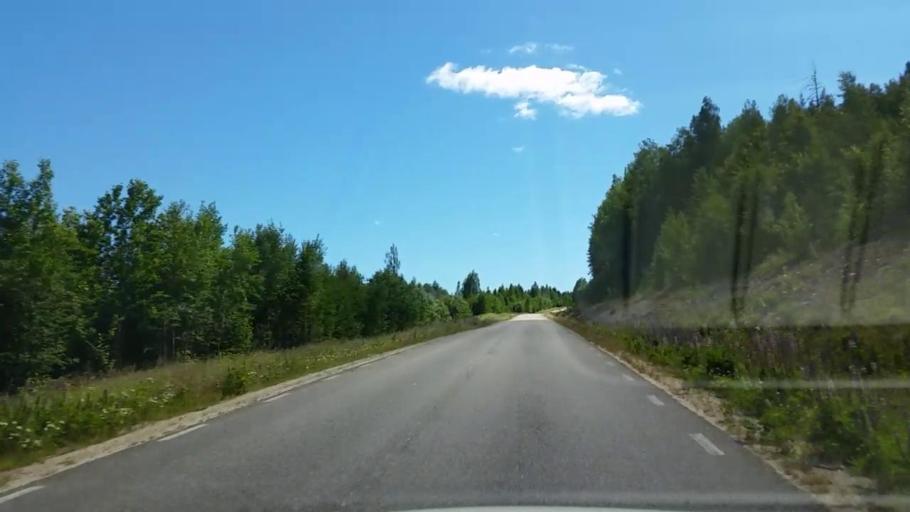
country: SE
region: Gaevleborg
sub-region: Ljusdals Kommun
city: Farila
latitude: 61.6954
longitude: 15.6477
